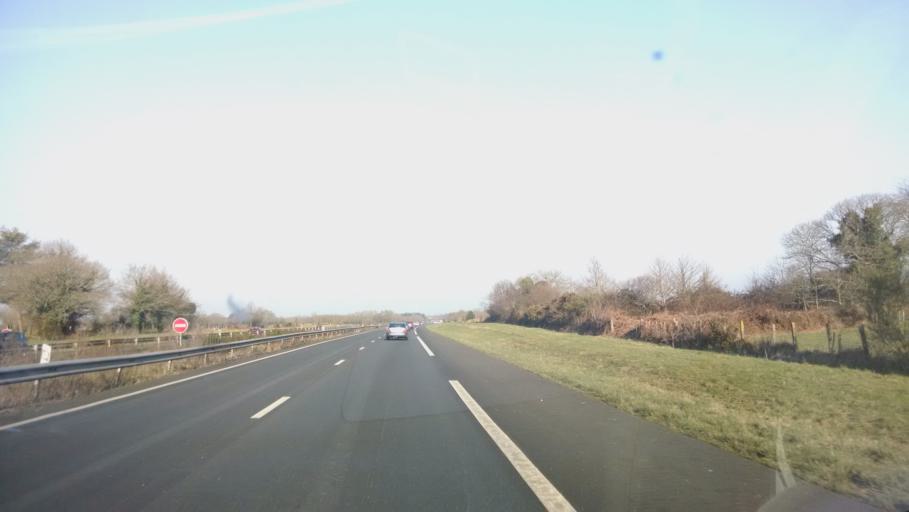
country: FR
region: Pays de la Loire
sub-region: Departement de la Loire-Atlantique
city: Le Temple-de-Bretagne
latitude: 47.3113
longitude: -1.7665
